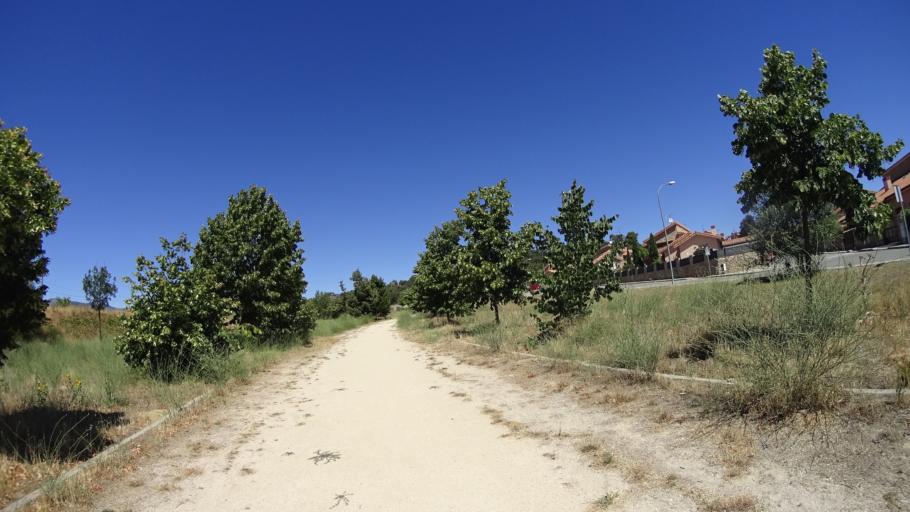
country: ES
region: Madrid
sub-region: Provincia de Madrid
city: Alpedrete
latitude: 40.6486
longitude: -4.0283
